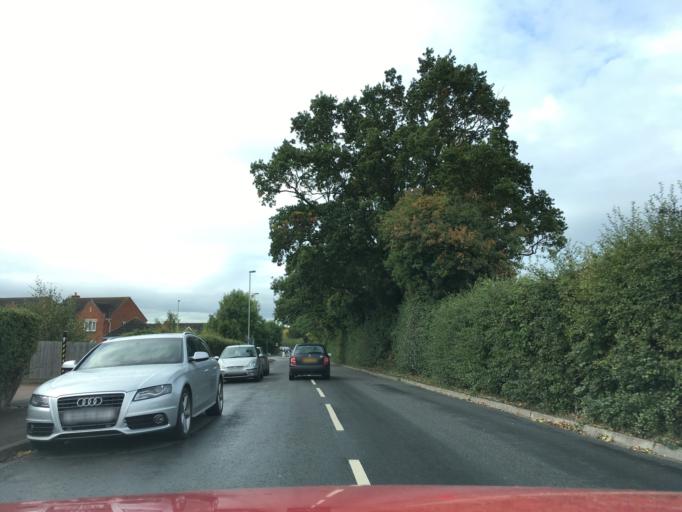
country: GB
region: England
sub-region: Gloucestershire
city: Uckington
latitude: 51.9018
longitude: -2.1277
